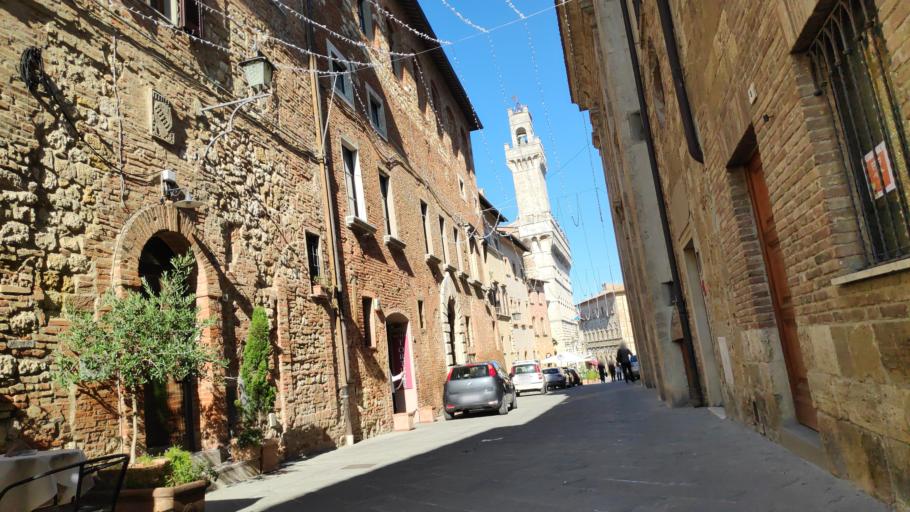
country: IT
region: Tuscany
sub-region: Provincia di Siena
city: Montepulciano
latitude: 43.0921
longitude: 11.7810
